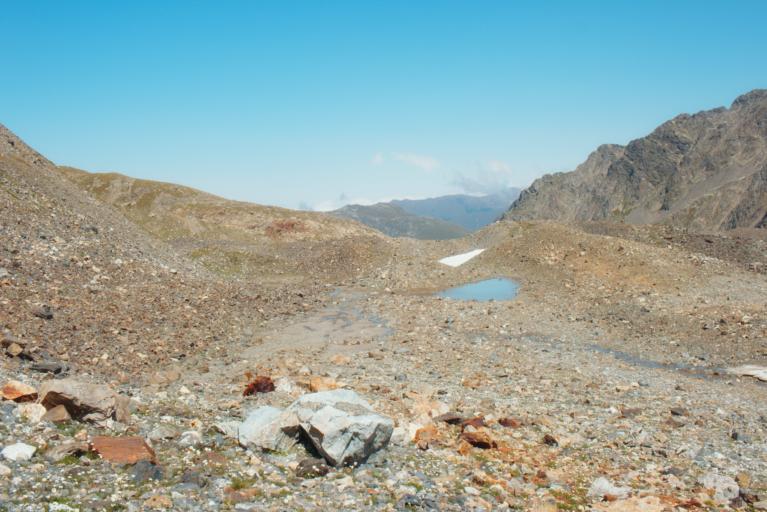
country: RU
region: Karachayevo-Cherkesiya
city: Nizhniy Arkhyz
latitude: 43.4267
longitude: 41.2486
